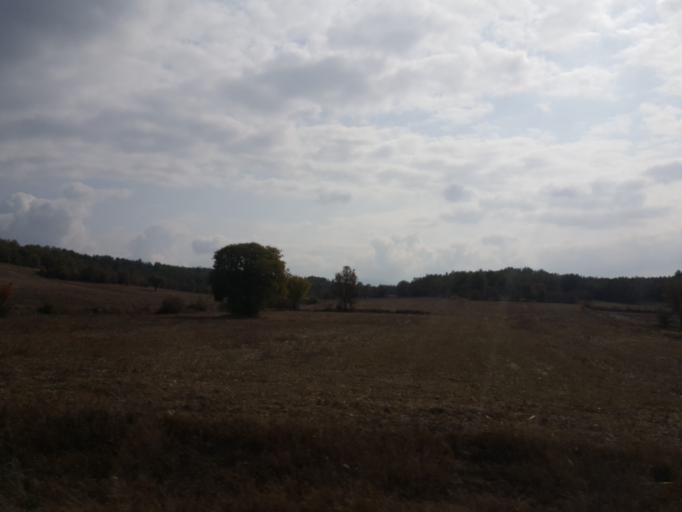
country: TR
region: Sinop
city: Sarayduzu
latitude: 41.3372
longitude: 34.8667
